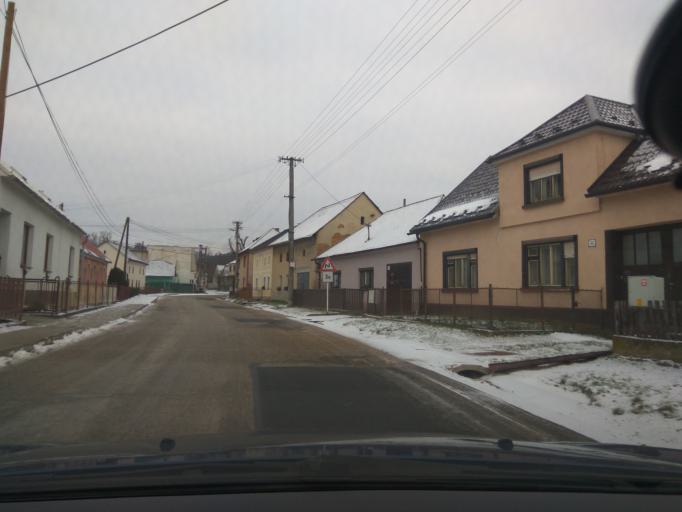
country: SK
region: Nitriansky
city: Stara Tura
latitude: 48.7872
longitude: 17.7347
